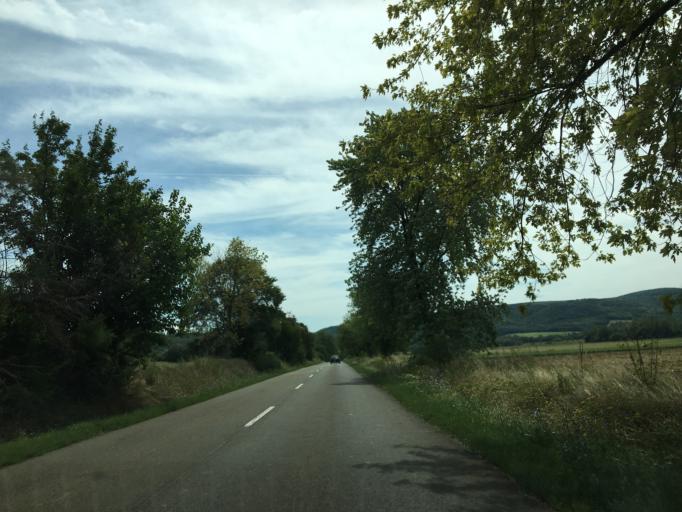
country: HU
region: Komarom-Esztergom
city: Esztergom
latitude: 47.8807
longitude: 18.7797
